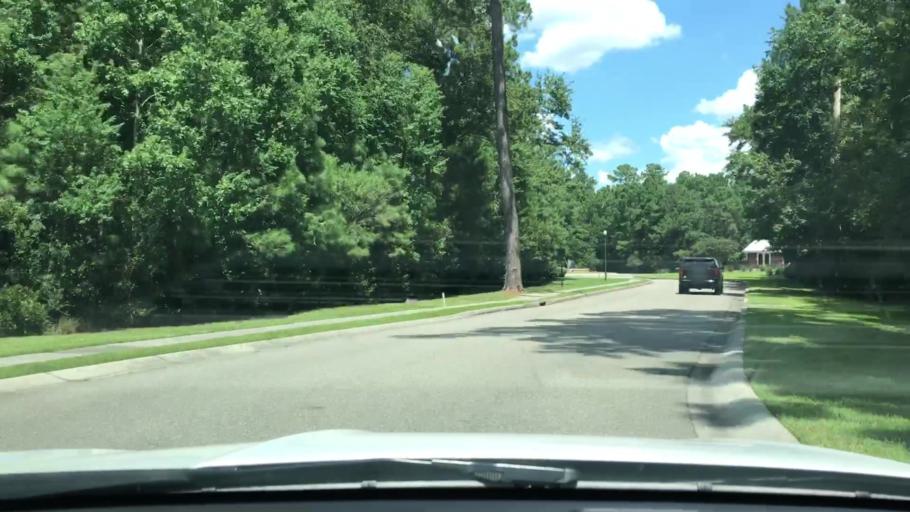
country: US
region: South Carolina
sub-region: Berkeley County
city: Hanahan
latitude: 32.9298
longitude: -79.9998
